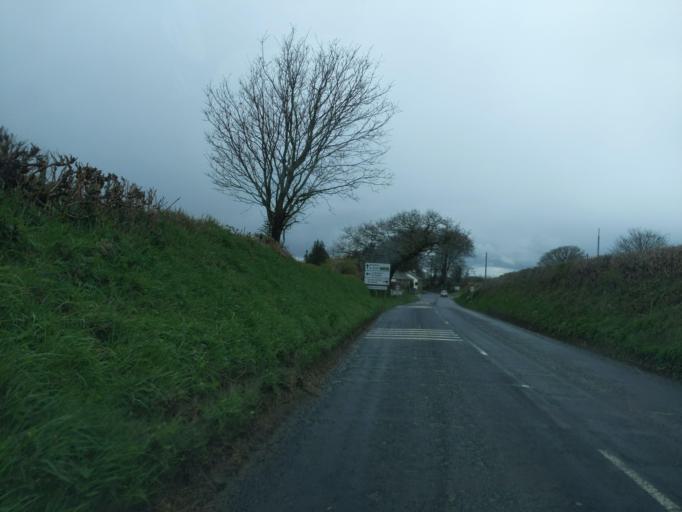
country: GB
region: England
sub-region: Cornwall
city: North Hill
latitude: 50.5785
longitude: -4.4260
